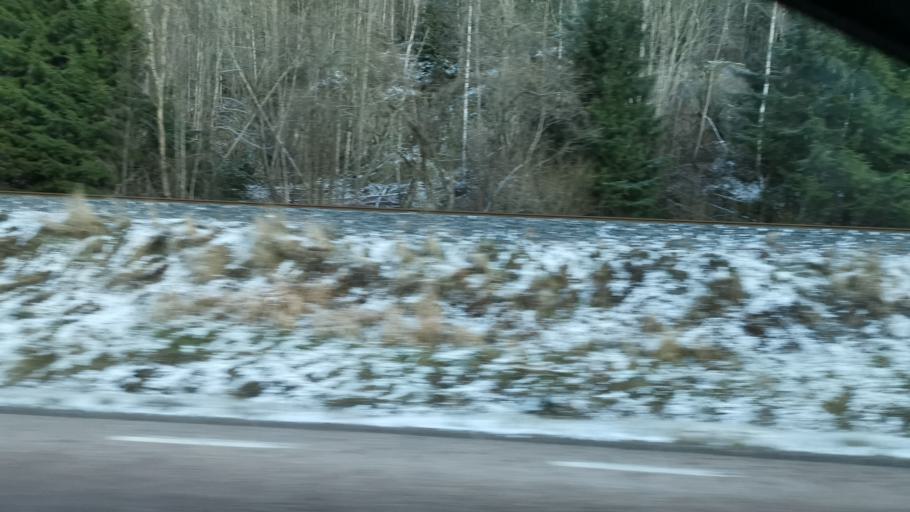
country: SE
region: Vaestra Goetaland
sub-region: Munkedals Kommun
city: Munkedal
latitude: 58.4154
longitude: 11.7327
